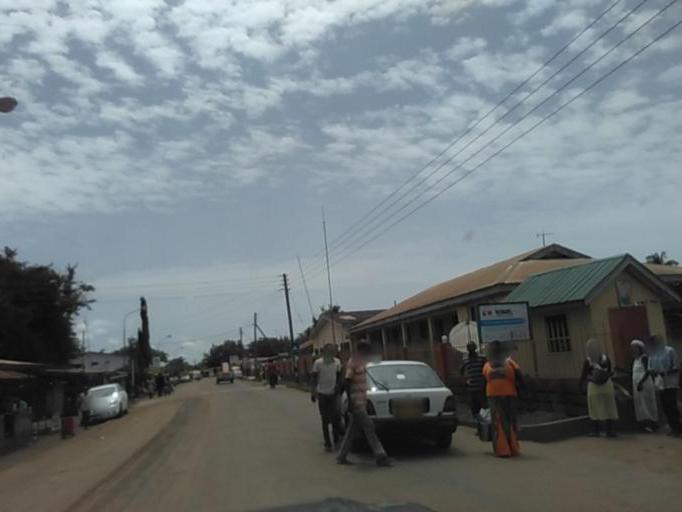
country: GH
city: Akropong
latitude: 6.0979
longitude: 0.1246
